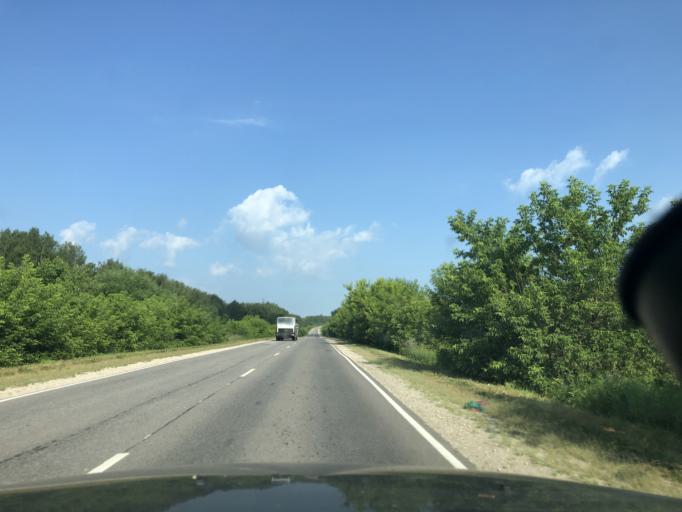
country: RU
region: Tula
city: Dubna
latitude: 54.1114
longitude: 37.0976
